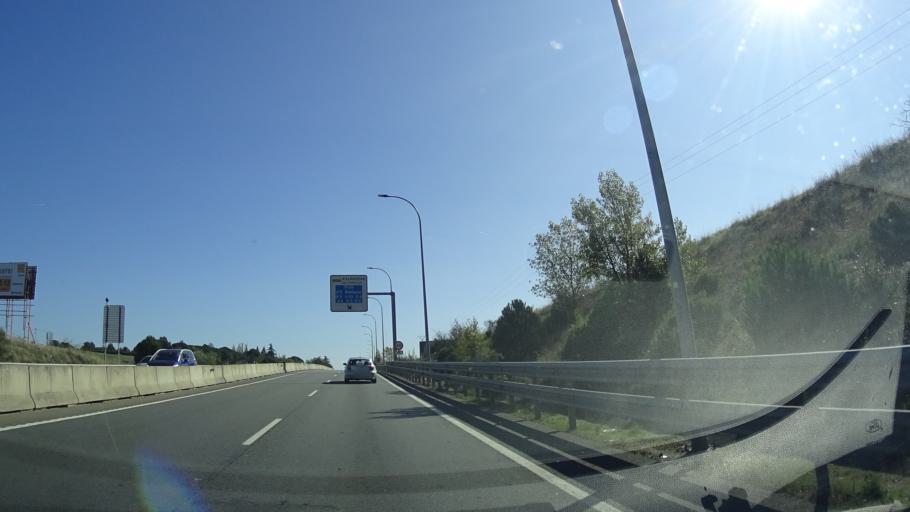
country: ES
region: Madrid
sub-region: Provincia de Madrid
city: Las Rozas de Madrid
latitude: 40.5025
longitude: -3.9044
